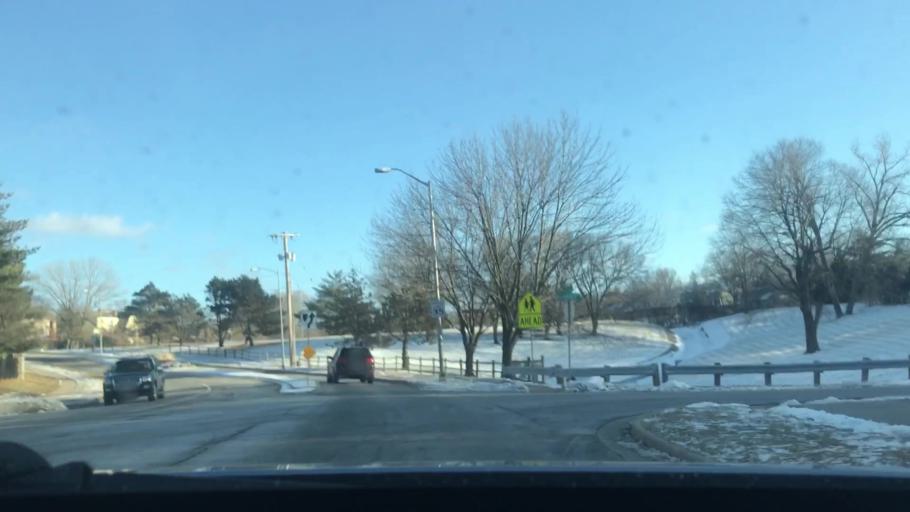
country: US
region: Kansas
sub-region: Johnson County
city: Lenexa
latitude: 38.9933
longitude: -94.7375
